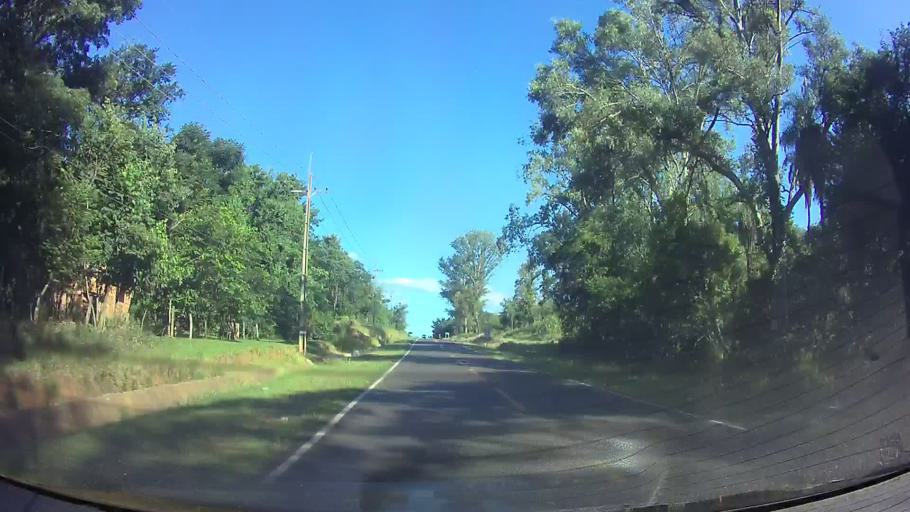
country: PY
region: Cordillera
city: Atyra
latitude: -25.3087
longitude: -57.1533
